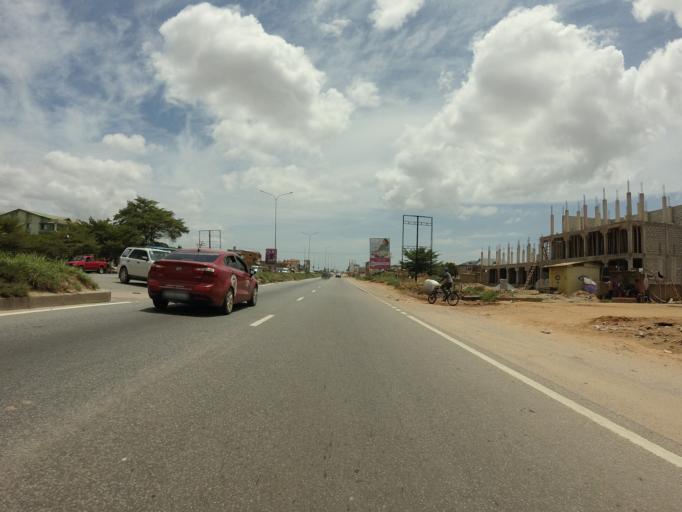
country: GH
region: Greater Accra
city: Gbawe
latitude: 5.5486
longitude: -0.3504
